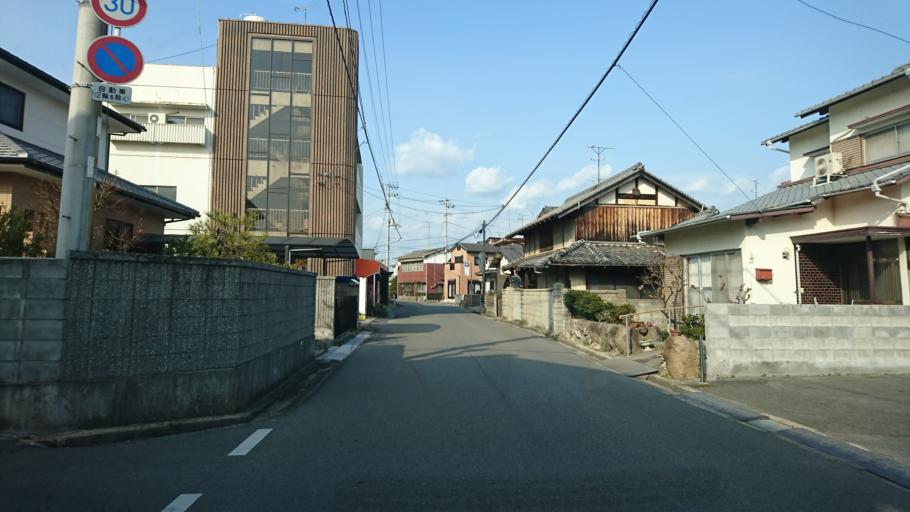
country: JP
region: Ehime
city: Saijo
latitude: 34.0225
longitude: 133.0392
